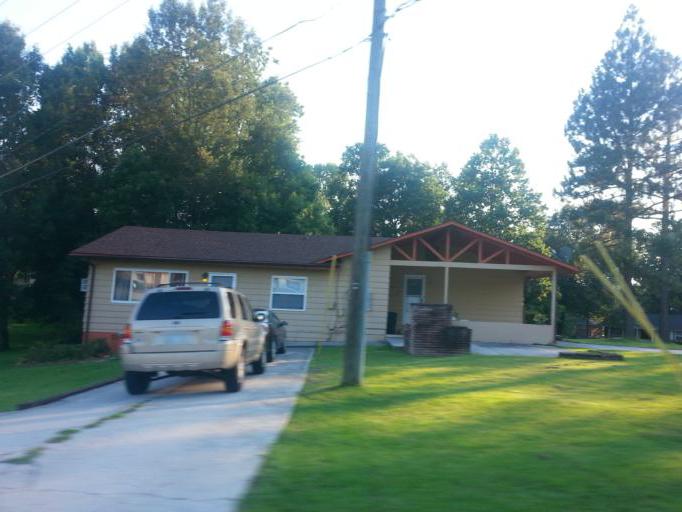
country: US
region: Tennessee
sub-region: Knox County
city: Knoxville
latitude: 35.9783
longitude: -83.9736
